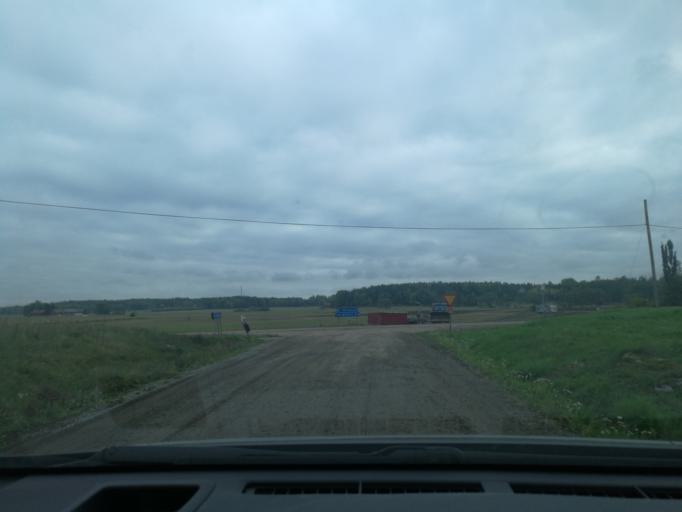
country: SE
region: Vaestmanland
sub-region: Vasteras
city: Tillberga
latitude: 59.7363
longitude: 16.7045
